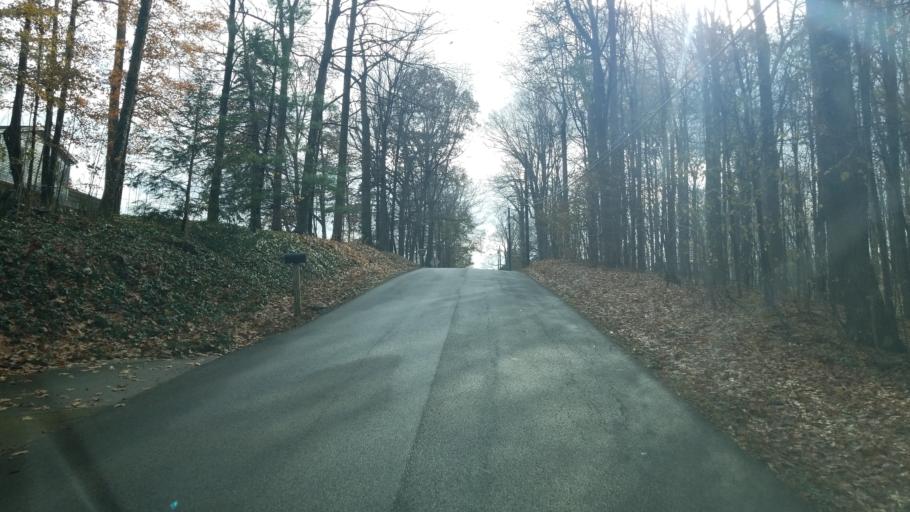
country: US
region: Ohio
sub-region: Richland County
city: Lincoln Heights
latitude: 40.8017
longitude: -82.4747
